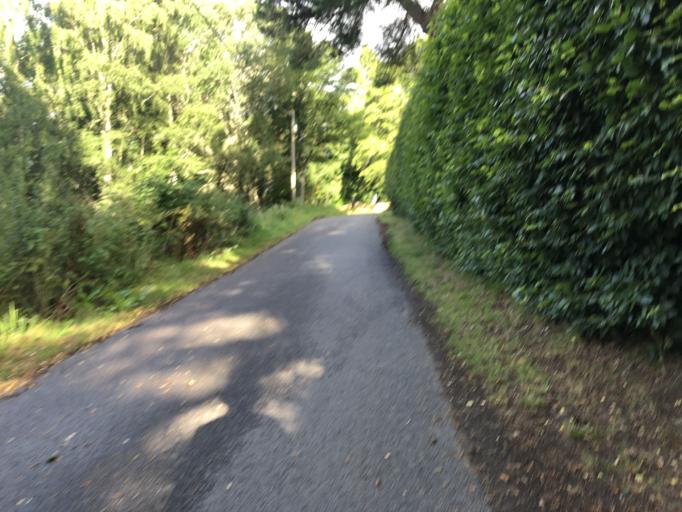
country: GB
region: Scotland
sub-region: Highland
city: Kingussie
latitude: 57.0664
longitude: -4.1274
